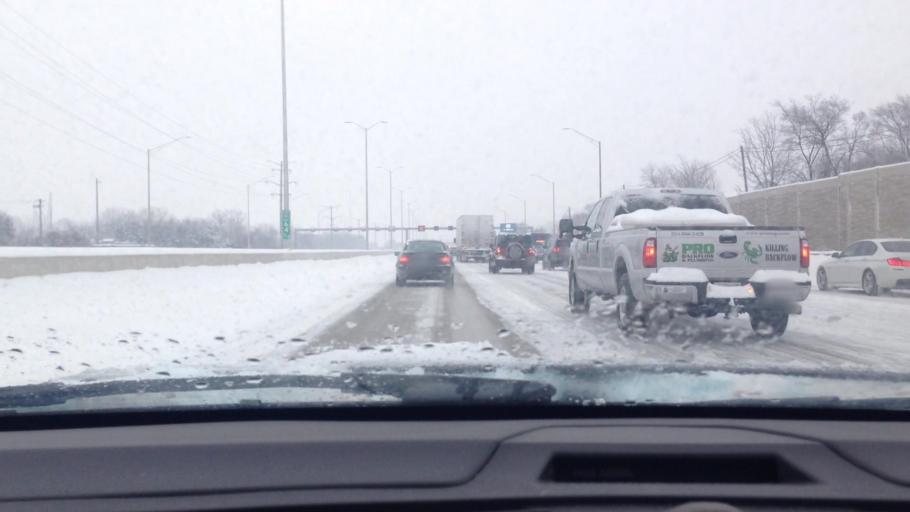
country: US
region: Illinois
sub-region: Cook County
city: Hoffman Estates
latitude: 42.0633
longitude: -88.0991
